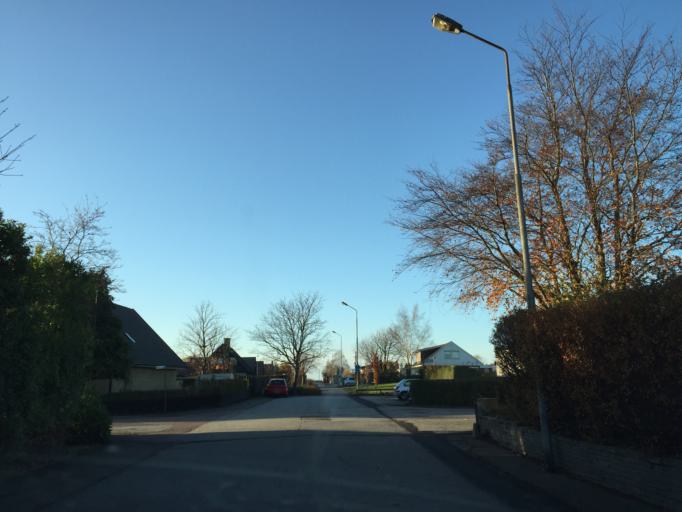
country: SE
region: Skane
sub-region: Staffanstorps Kommun
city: Hjaerup
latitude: 55.6691
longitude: 13.1357
